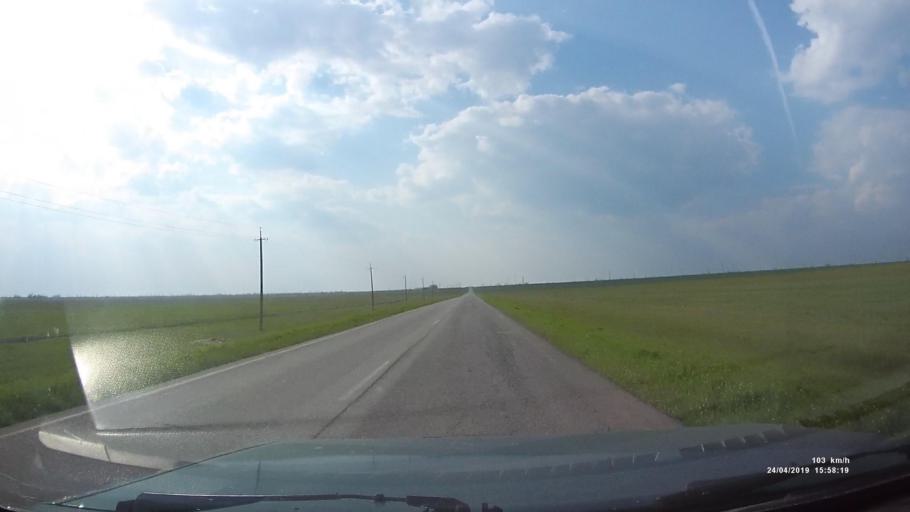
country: RU
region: Kalmykiya
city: Yashalta
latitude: 46.6130
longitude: 42.4924
